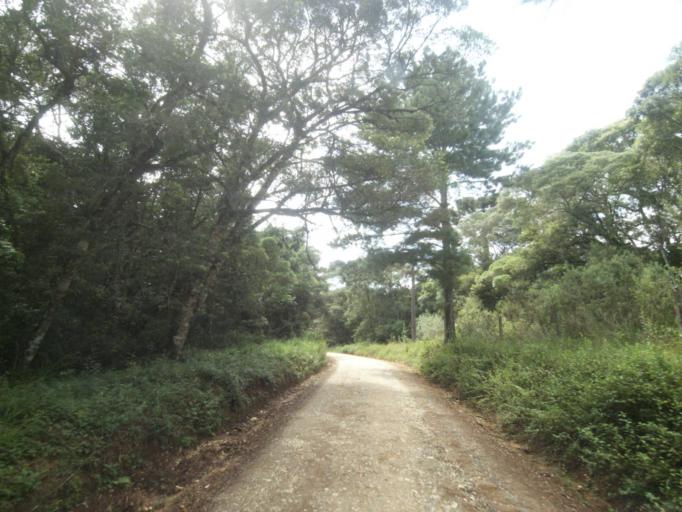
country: BR
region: Parana
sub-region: Campina Grande Do Sul
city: Campina Grande do Sul
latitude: -25.3220
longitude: -49.0692
